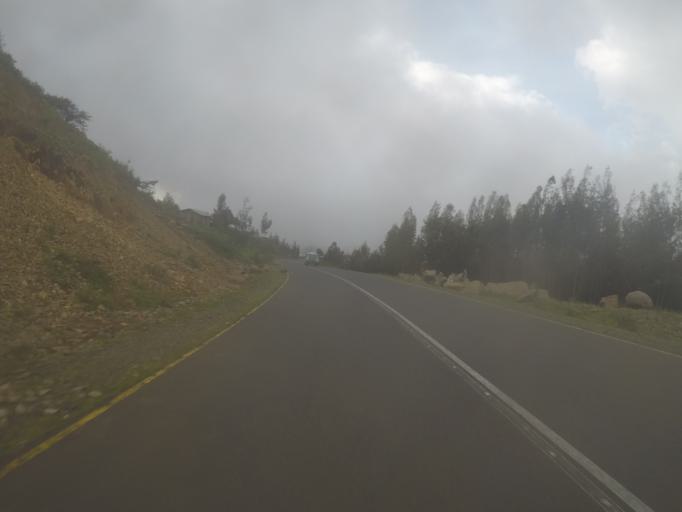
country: ET
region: Amhara
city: Gondar
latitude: 12.7312
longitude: 37.5171
